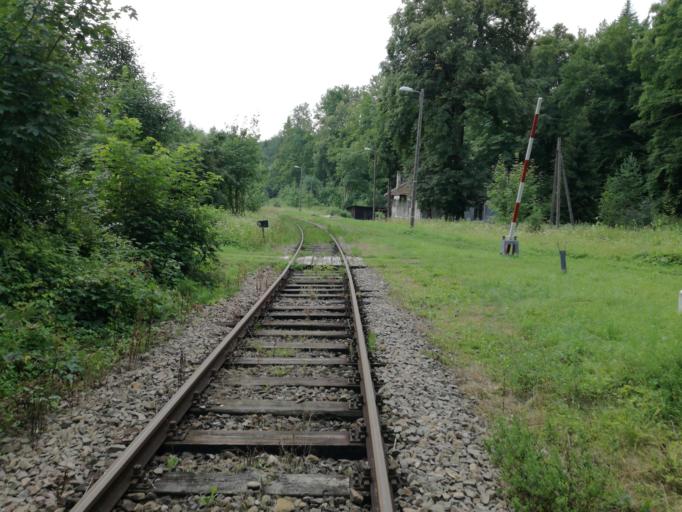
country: PL
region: Subcarpathian Voivodeship
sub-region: Powiat leski
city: Uherce Mineralne
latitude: 49.4644
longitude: 22.3797
